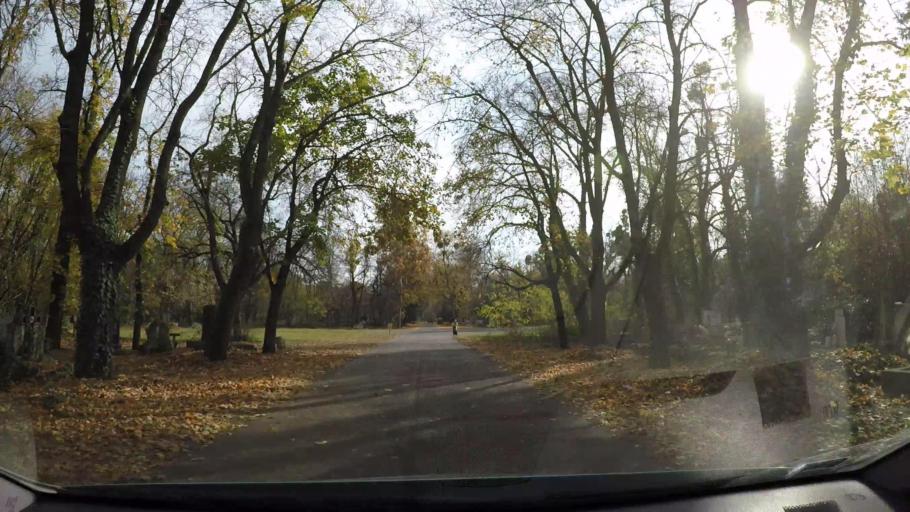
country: HU
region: Budapest
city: Budapest XVIII. keruelet
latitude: 47.4689
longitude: 19.1881
